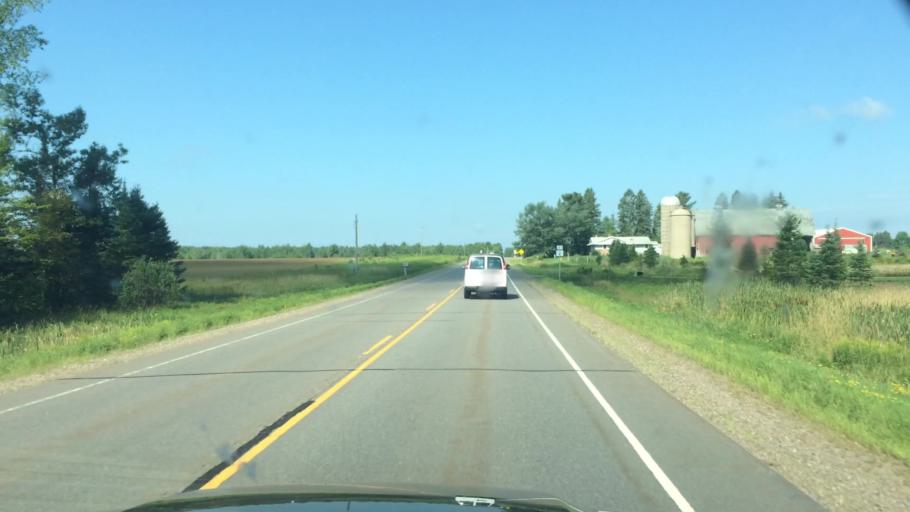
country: US
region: Wisconsin
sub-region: Lincoln County
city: Merrill
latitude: 45.1484
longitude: -89.4585
